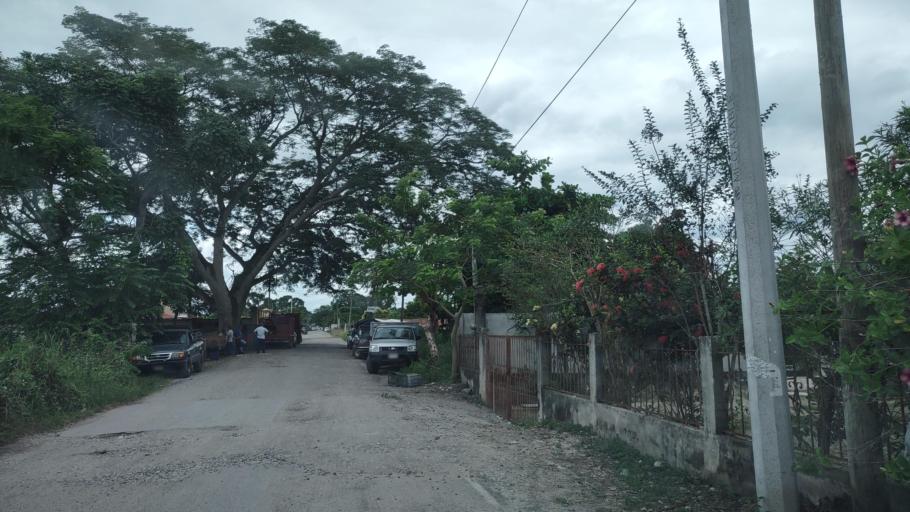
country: MX
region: Veracruz
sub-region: Martinez de la Torre
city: El Progreso
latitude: 20.0960
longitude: -97.0107
